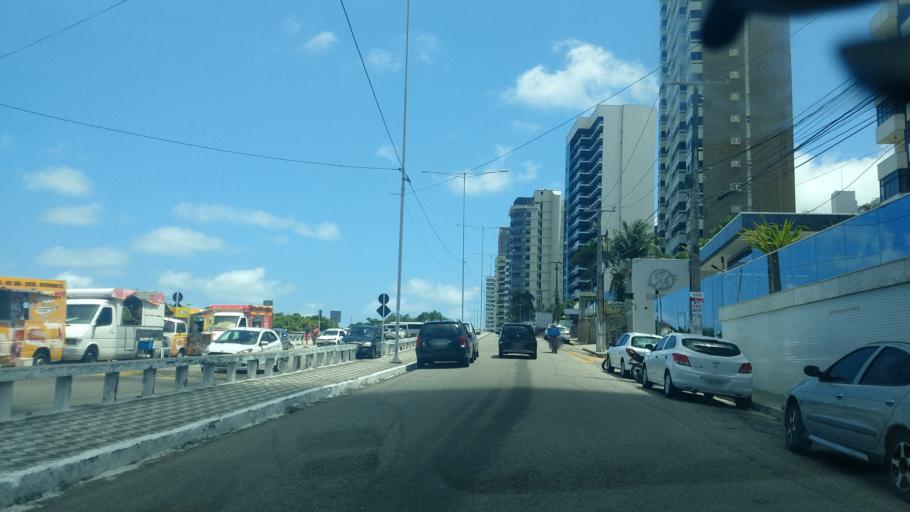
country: BR
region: Rio Grande do Norte
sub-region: Natal
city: Natal
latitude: -5.7808
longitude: -35.1961
